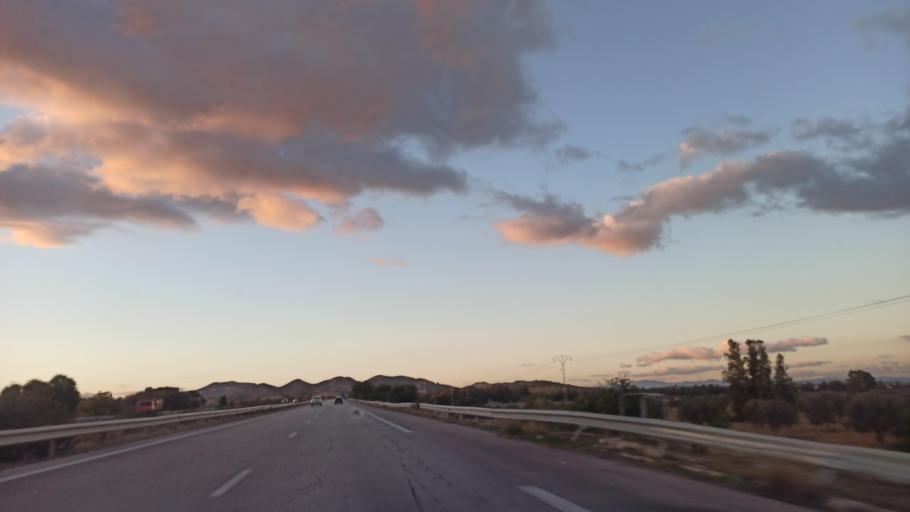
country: TN
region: Susah
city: Harqalah
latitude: 36.2108
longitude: 10.4261
